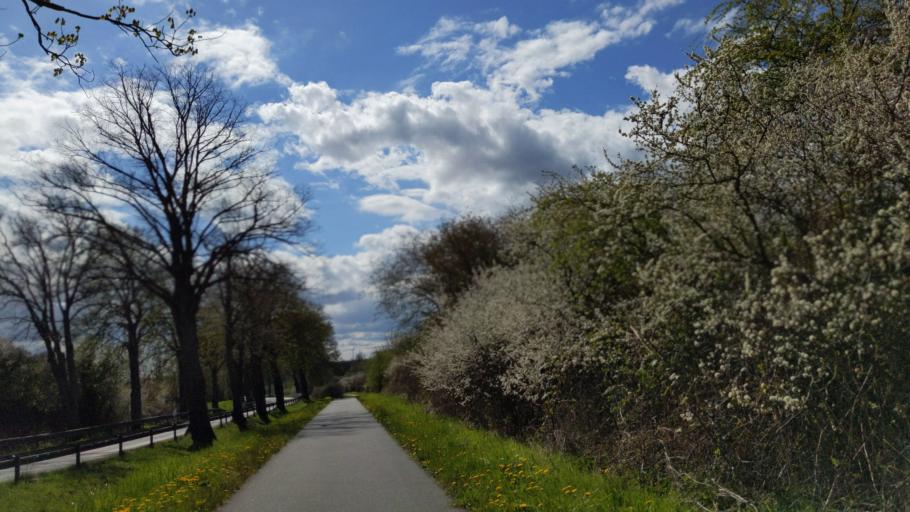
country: DE
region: Mecklenburg-Vorpommern
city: Dassow
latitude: 53.9016
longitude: 10.9453
